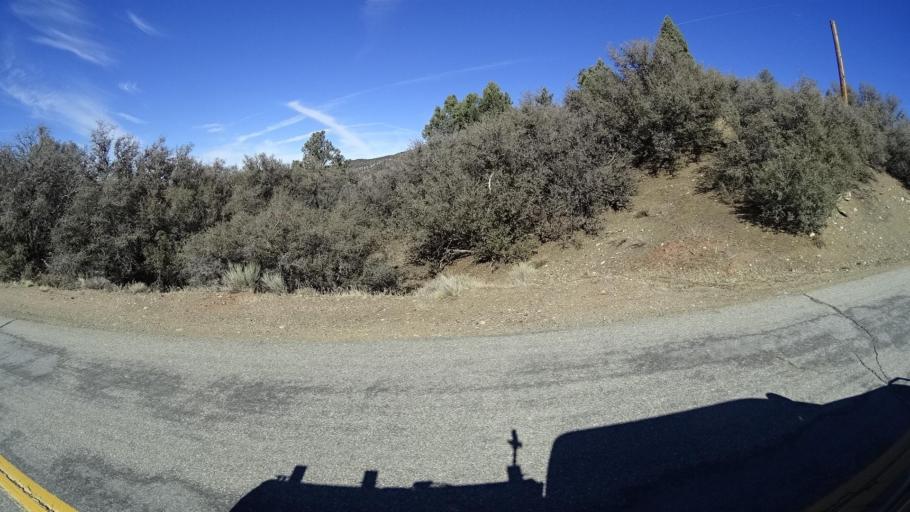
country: US
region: California
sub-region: Kern County
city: Pine Mountain Club
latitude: 34.8652
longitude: -119.2401
